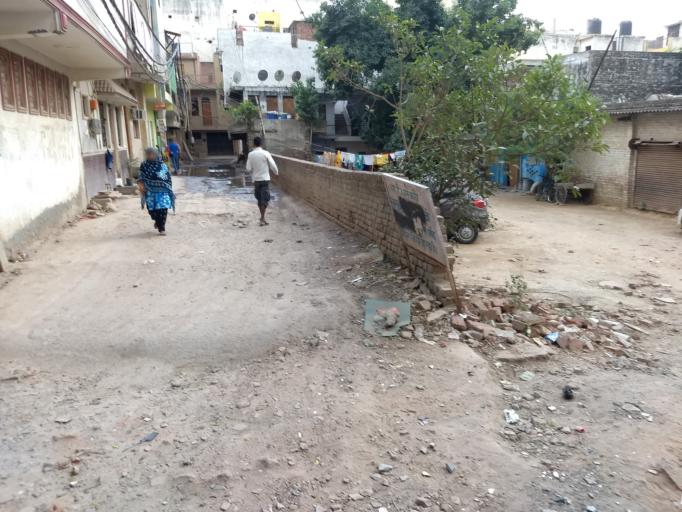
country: IN
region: NCT
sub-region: Central Delhi
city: Karol Bagh
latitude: 28.5413
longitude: 77.1281
